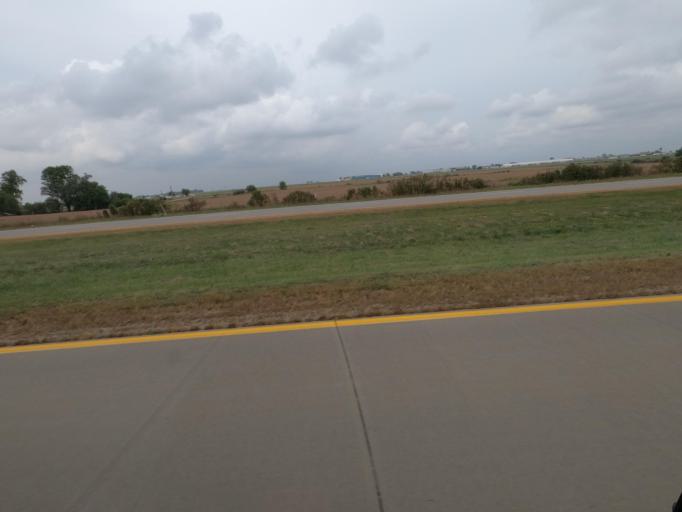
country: US
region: Iowa
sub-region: Wapello County
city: Ottumwa
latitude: 41.0948
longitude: -92.4470
